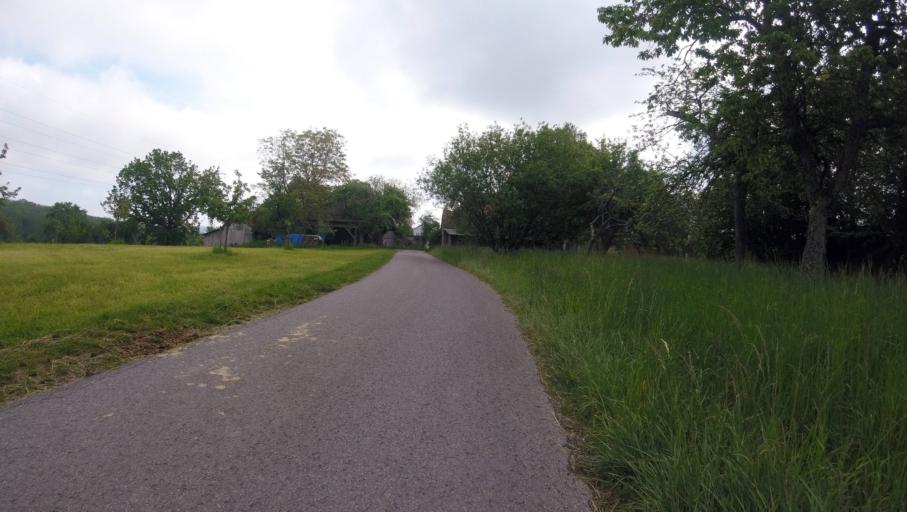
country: DE
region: Baden-Wuerttemberg
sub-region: Regierungsbezirk Stuttgart
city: Backnang
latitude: 48.9405
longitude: 9.4703
